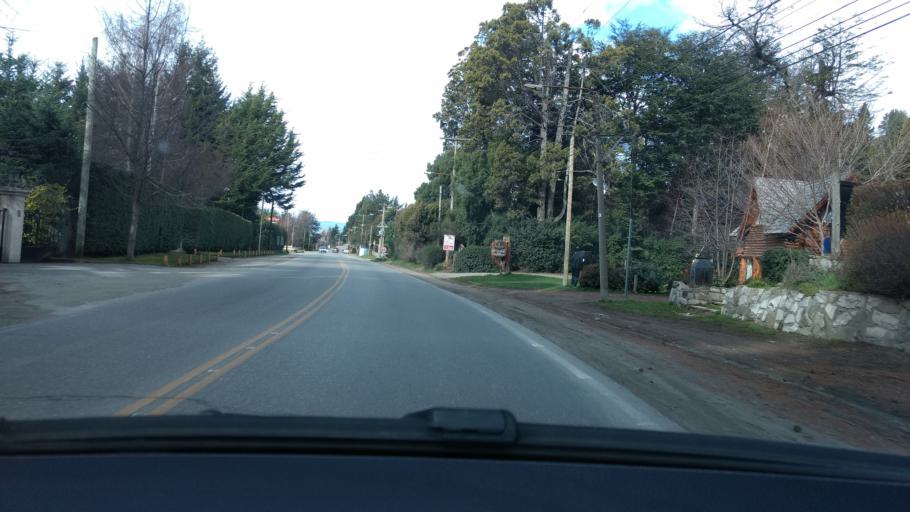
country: AR
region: Rio Negro
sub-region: Departamento de Bariloche
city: San Carlos de Bariloche
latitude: -41.1214
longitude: -71.3753
